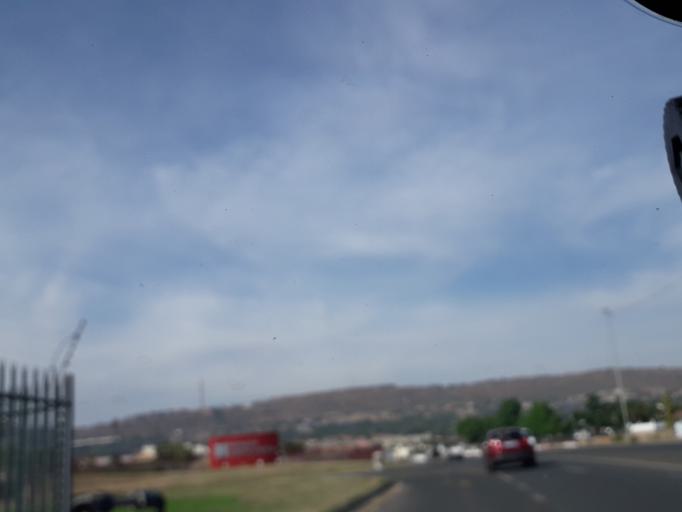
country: ZA
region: Gauteng
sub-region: West Rand District Municipality
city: Muldersdriseloop
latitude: -26.0826
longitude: 27.8753
